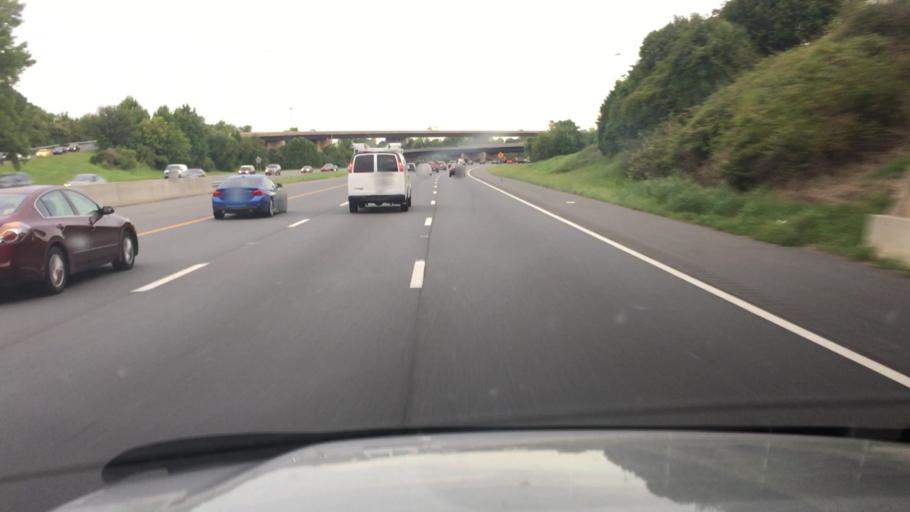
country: US
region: North Carolina
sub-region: Mecklenburg County
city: Pineville
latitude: 35.1235
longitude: -80.9130
